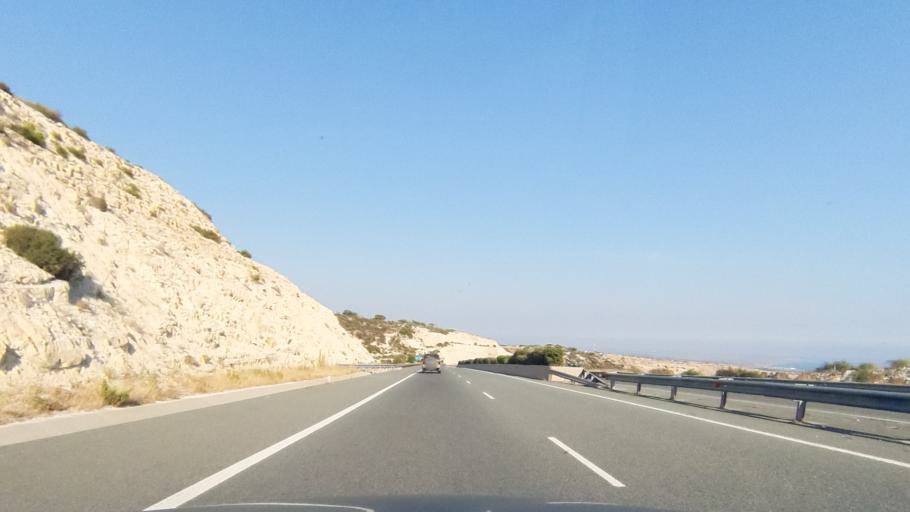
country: CY
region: Limassol
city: Sotira
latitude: 34.6929
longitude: 32.8659
